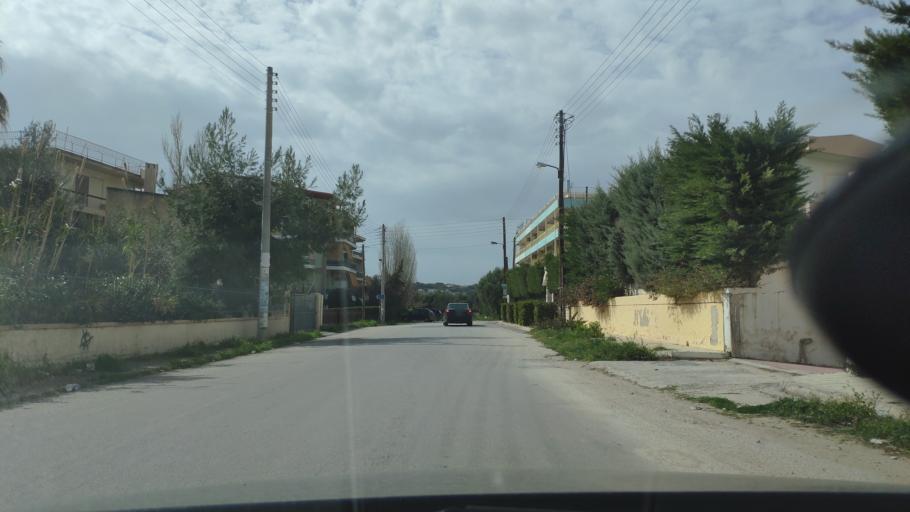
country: GR
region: Attica
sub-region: Nomarchia Anatolikis Attikis
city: Limin Mesoyaias
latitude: 37.8954
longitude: 24.0122
